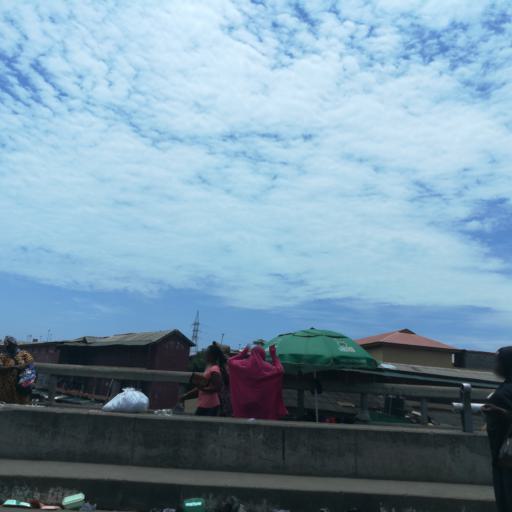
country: NG
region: Lagos
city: Lagos
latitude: 6.4637
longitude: 3.3862
